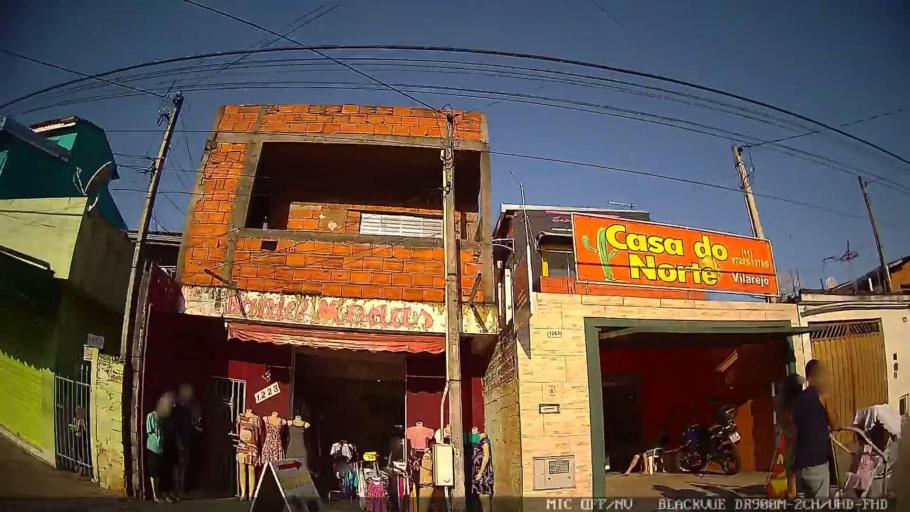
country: BR
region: Sao Paulo
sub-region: Cabreuva
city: Cabreuva
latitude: -23.2658
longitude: -47.0577
